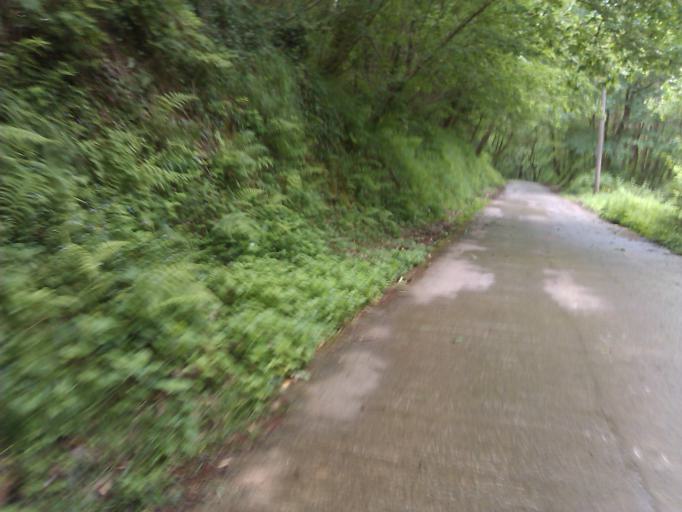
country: ES
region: Basque Country
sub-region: Provincia de Guipuzcoa
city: Andoain
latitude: 43.2020
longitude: -2.0088
